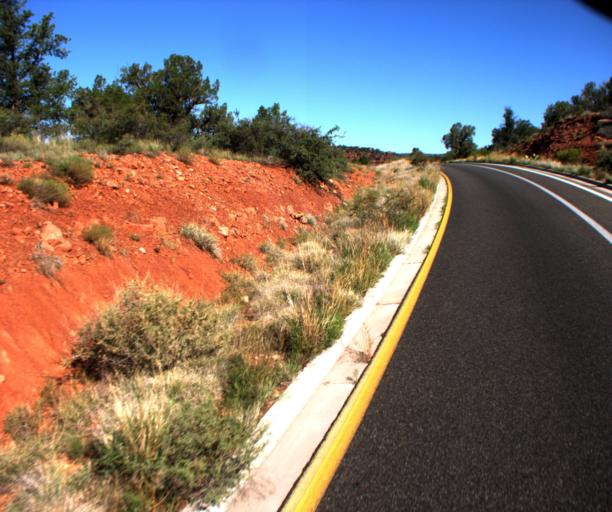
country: US
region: Arizona
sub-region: Yavapai County
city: Village of Oak Creek (Big Park)
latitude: 34.8213
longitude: -111.7728
